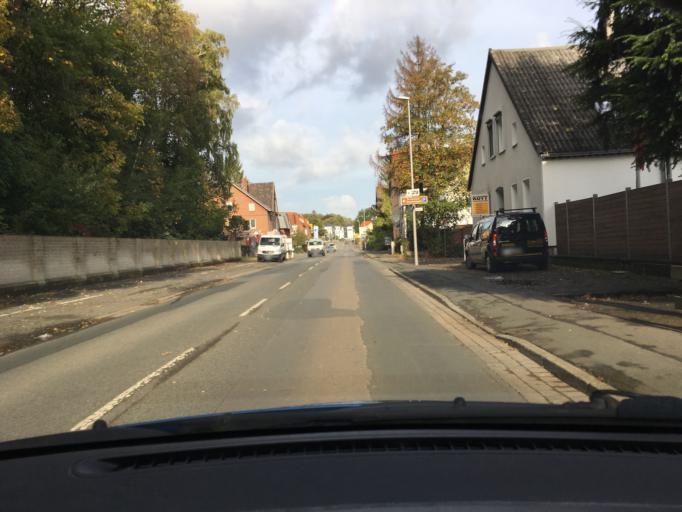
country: DE
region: Lower Saxony
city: Barsinghausen
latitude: 52.2996
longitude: 9.4732
